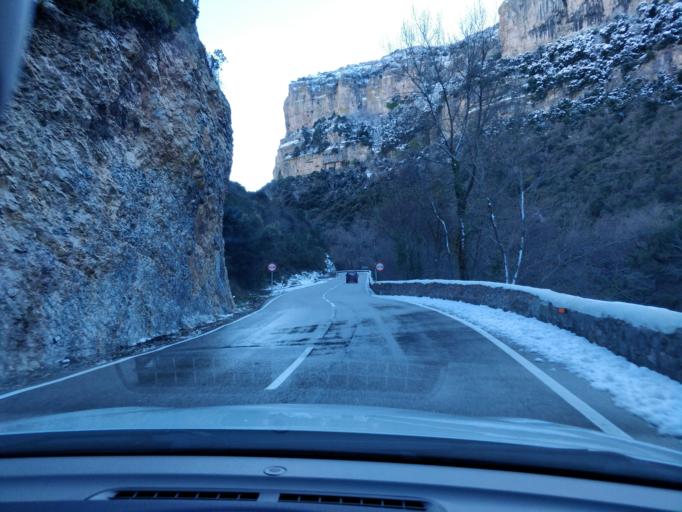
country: ES
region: Castille and Leon
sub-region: Provincia de Burgos
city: Medina de Pomar
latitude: 42.8733
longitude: -3.5959
